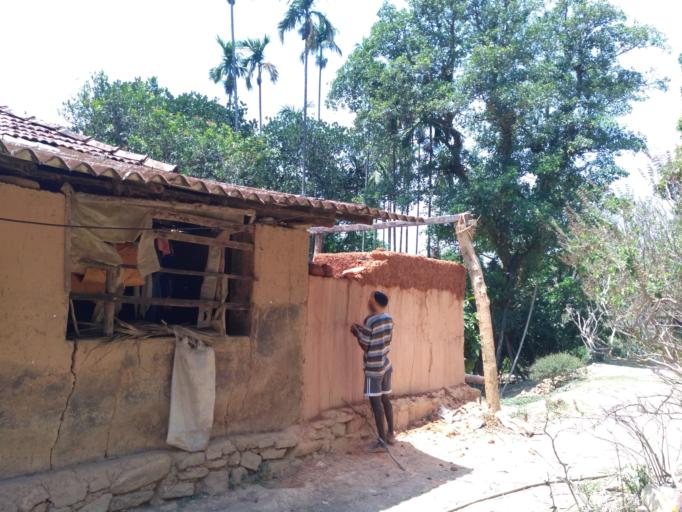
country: IN
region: Karnataka
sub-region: Kodagu
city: Somvarpet
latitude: 12.6693
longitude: 75.6527
